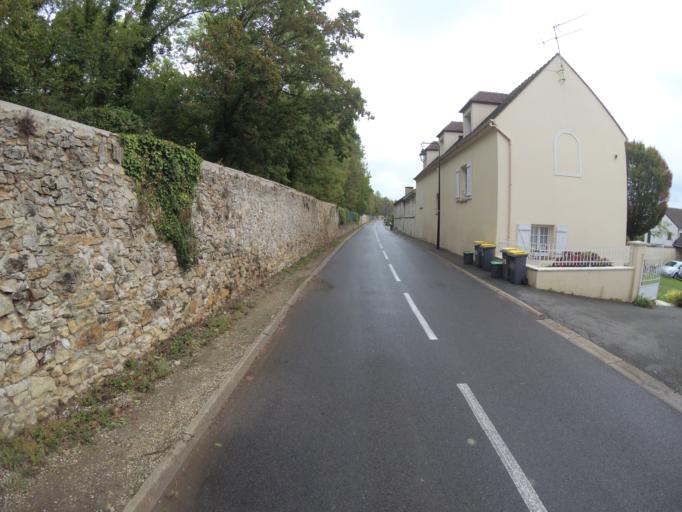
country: FR
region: Ile-de-France
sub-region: Departement de Seine-et-Marne
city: Gouvernes
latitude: 48.8488
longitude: 2.6930
